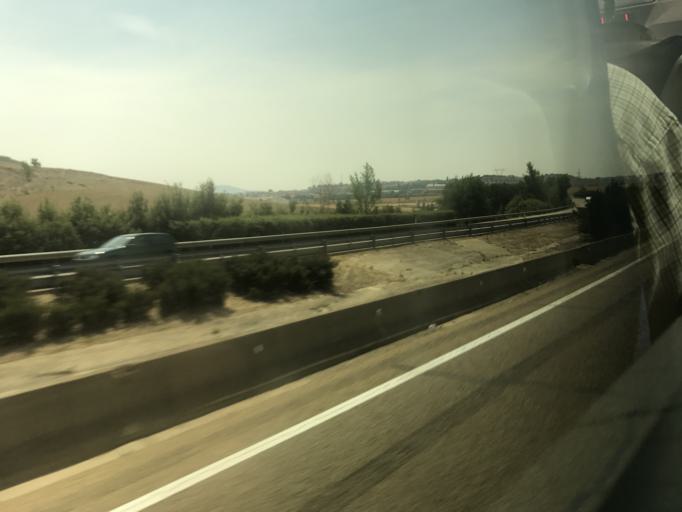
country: ES
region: Castille and Leon
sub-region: Provincia de Valladolid
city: Zaratan
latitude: 41.6718
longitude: -4.7621
